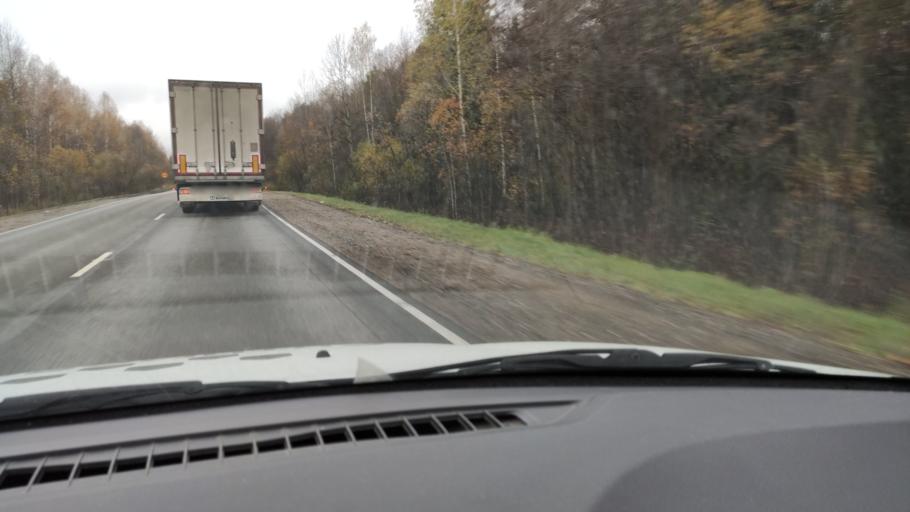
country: RU
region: Kirov
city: Slobodskoy
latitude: 58.7269
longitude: 50.2272
